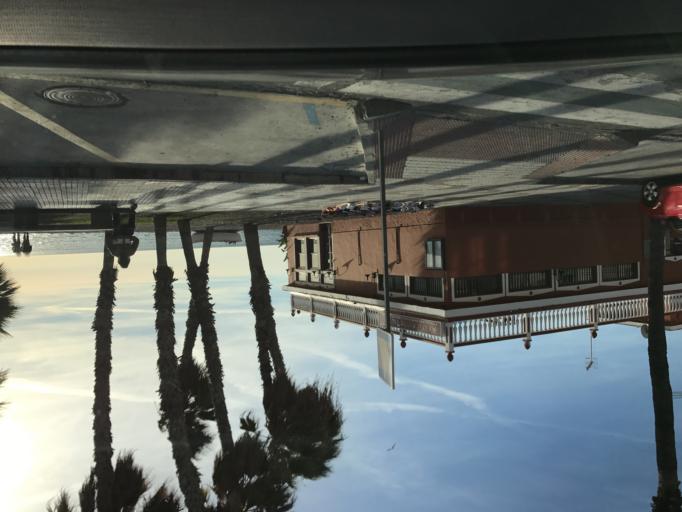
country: ES
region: Andalusia
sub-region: Provincia de Granada
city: Almunecar
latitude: 36.7301
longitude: -3.6959
